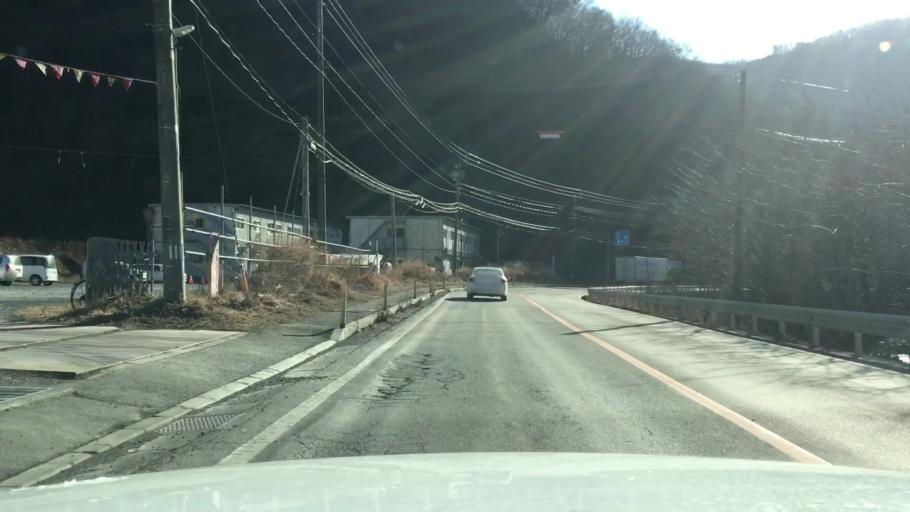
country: JP
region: Iwate
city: Miyako
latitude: 39.5927
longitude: 141.6643
